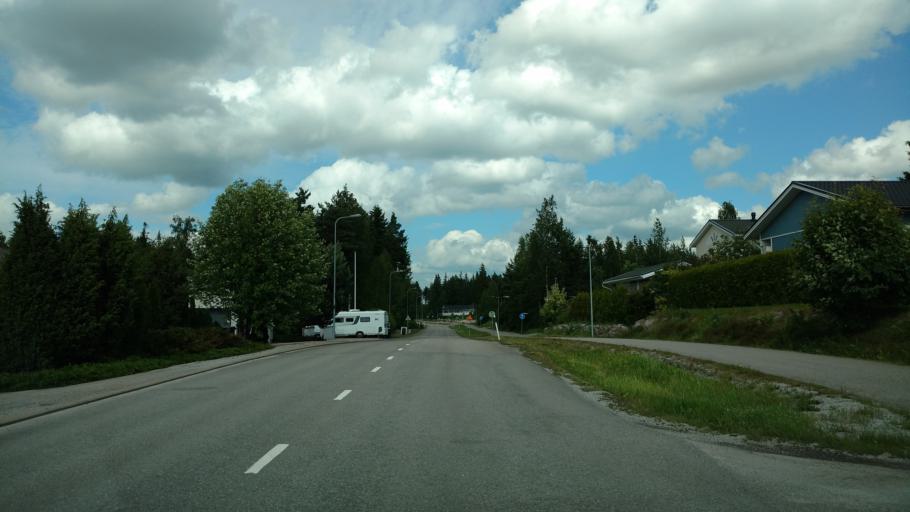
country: FI
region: Varsinais-Suomi
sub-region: Salo
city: Salo
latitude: 60.4027
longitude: 23.1804
